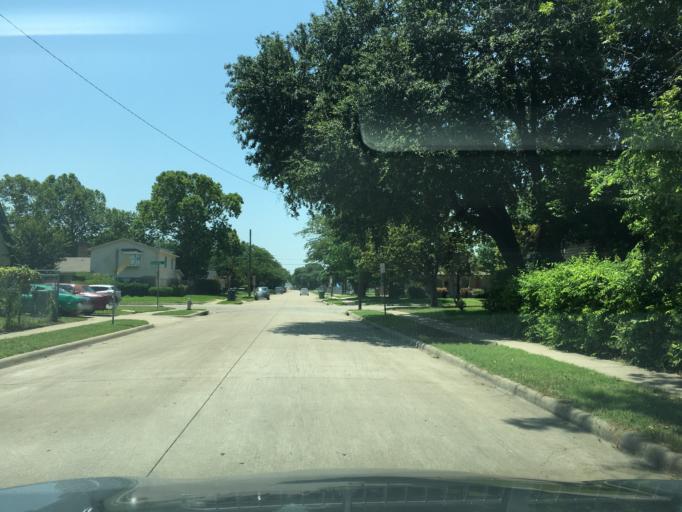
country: US
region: Texas
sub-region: Dallas County
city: Richardson
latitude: 32.9160
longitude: -96.6900
